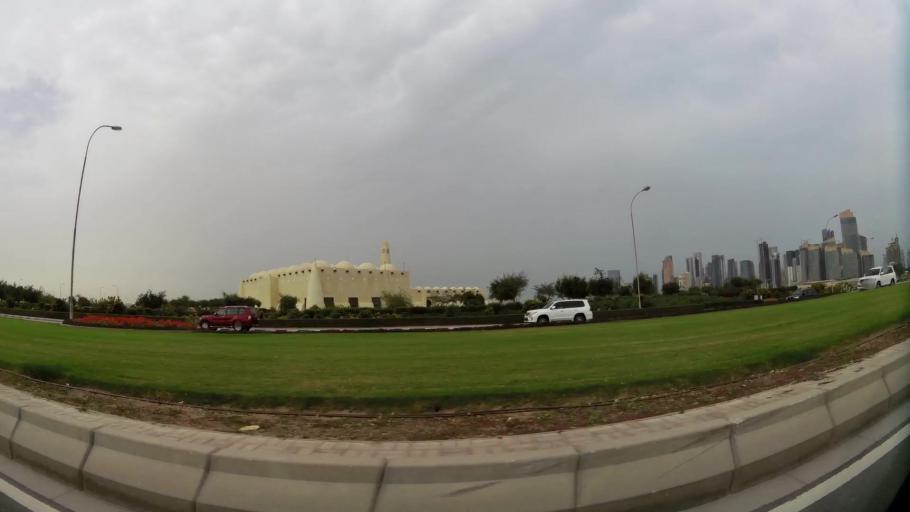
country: QA
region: Baladiyat ad Dawhah
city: Doha
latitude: 25.3142
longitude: 51.5044
